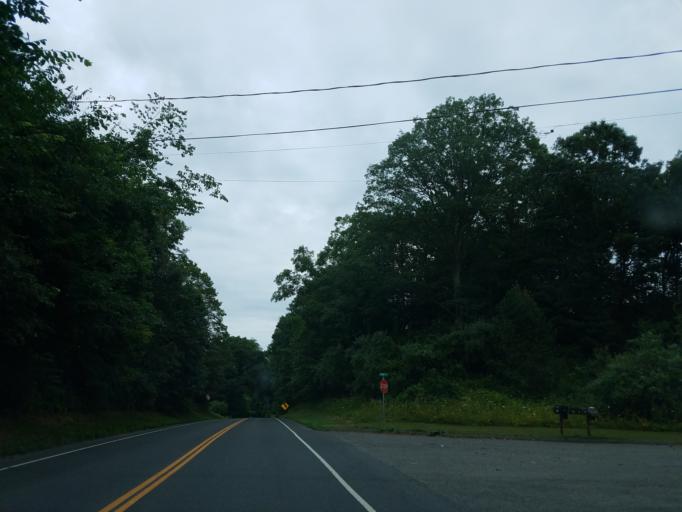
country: US
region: Connecticut
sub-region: Litchfield County
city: New Milford
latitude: 41.6224
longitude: -73.3962
